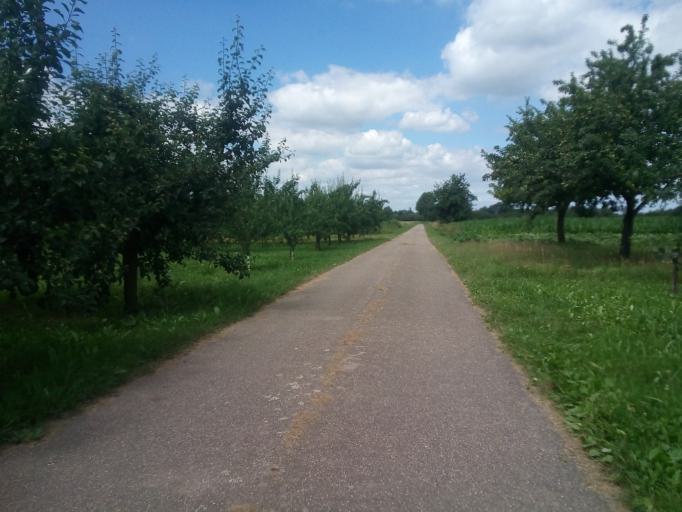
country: DE
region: Baden-Wuerttemberg
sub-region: Freiburg Region
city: Renchen
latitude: 48.6169
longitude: 7.9837
